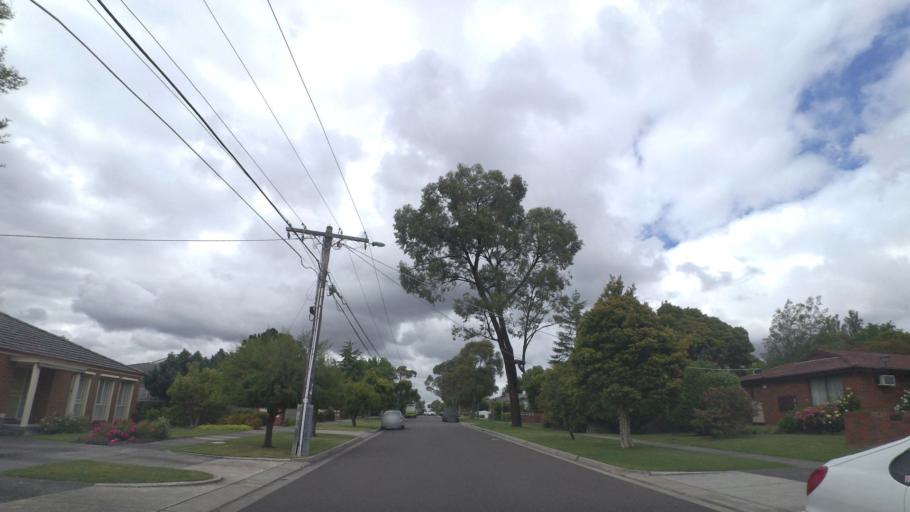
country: AU
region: Victoria
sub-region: Maroondah
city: Croydon North
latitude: -37.7874
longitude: 145.2847
